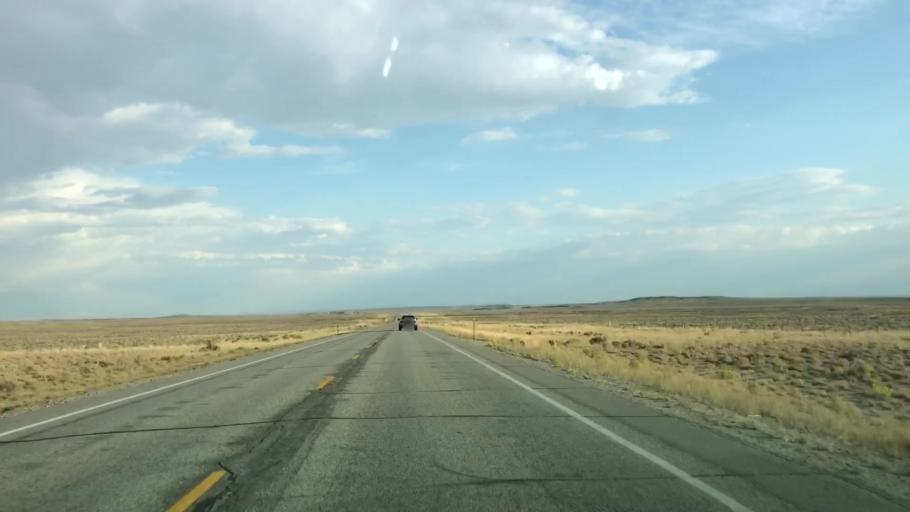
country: US
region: Wyoming
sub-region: Sublette County
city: Pinedale
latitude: 42.3873
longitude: -109.5384
